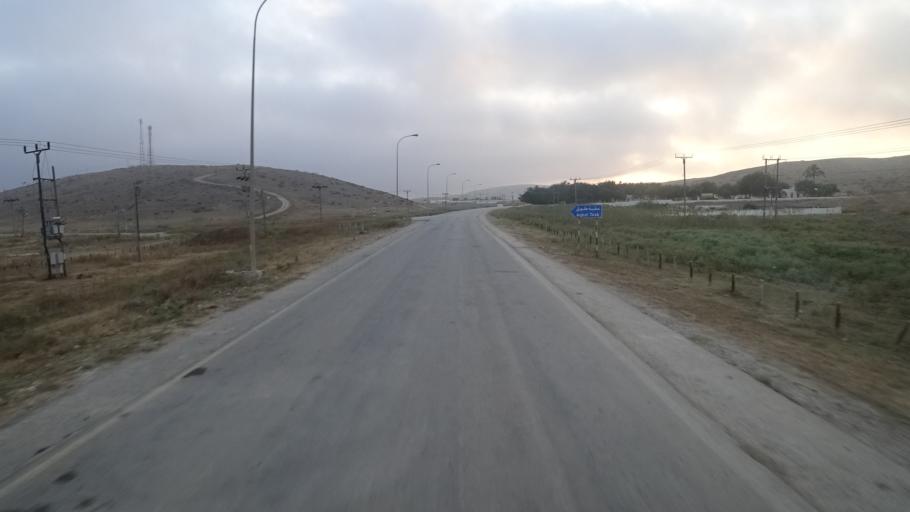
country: OM
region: Zufar
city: Salalah
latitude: 17.1240
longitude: 53.9406
